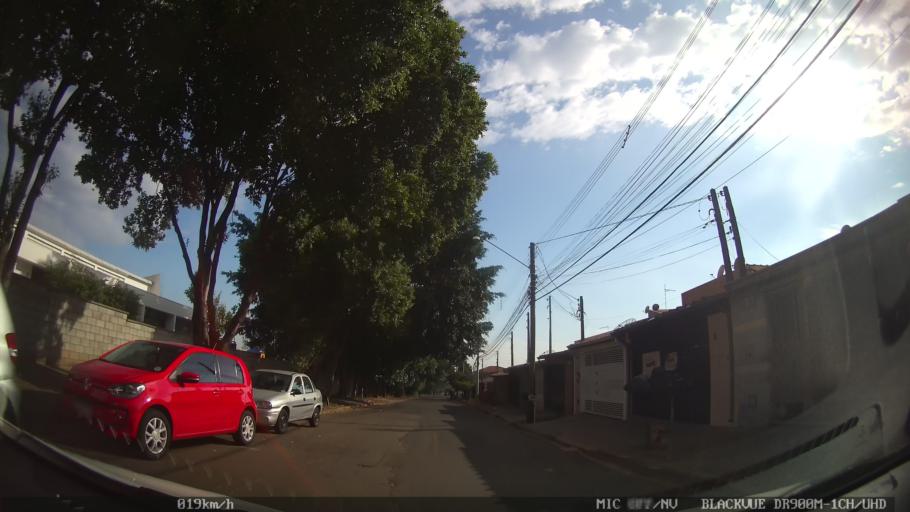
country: BR
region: Sao Paulo
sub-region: Americana
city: Americana
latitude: -22.7161
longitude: -47.3685
